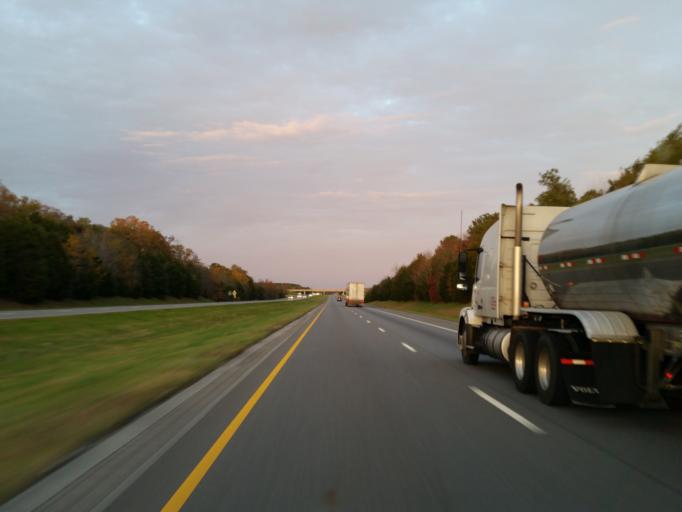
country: US
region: Alabama
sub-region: Sumter County
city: Livingston
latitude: 32.6932
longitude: -88.1508
